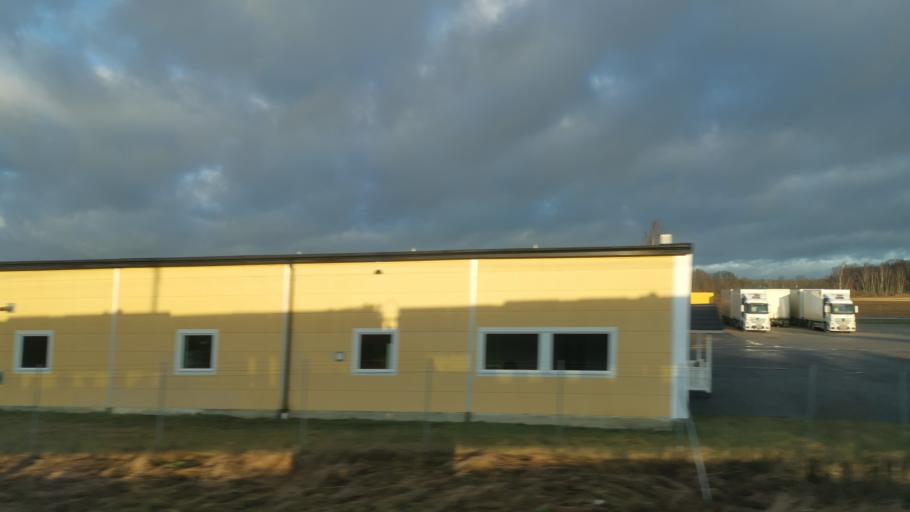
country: SE
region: Soedermanland
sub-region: Vingakers Kommun
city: Vingaker
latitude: 59.0456
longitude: 15.8951
